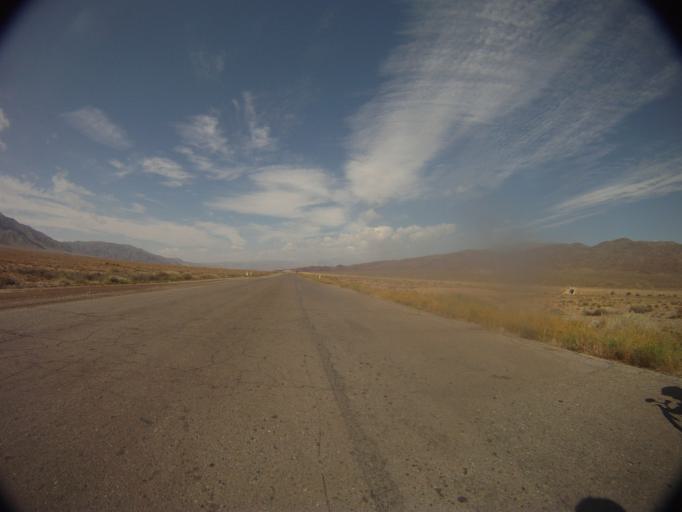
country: KG
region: Ysyk-Koel
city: Balykchy
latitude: 42.2920
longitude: 76.0592
